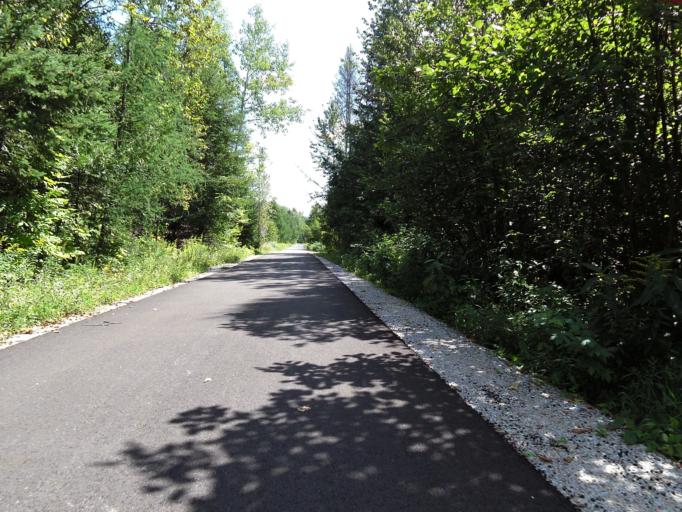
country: CA
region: Quebec
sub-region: Outaouais
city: Maniwaki
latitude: 46.1569
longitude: -76.0426
